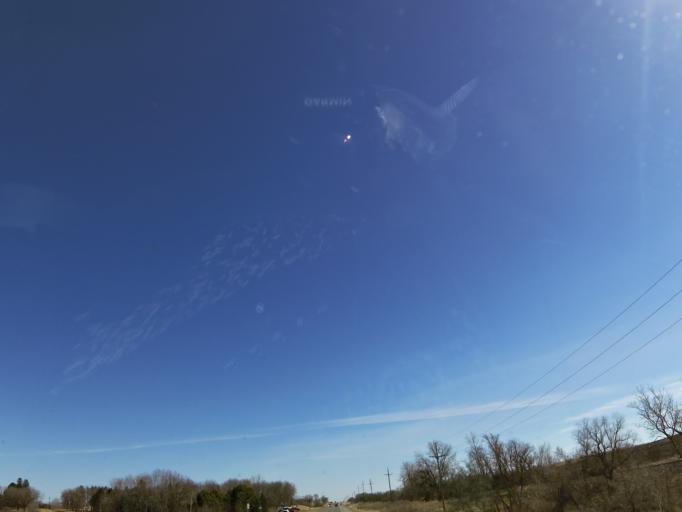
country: US
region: Minnesota
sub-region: Wright County
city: Buffalo
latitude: 45.2086
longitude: -93.9237
